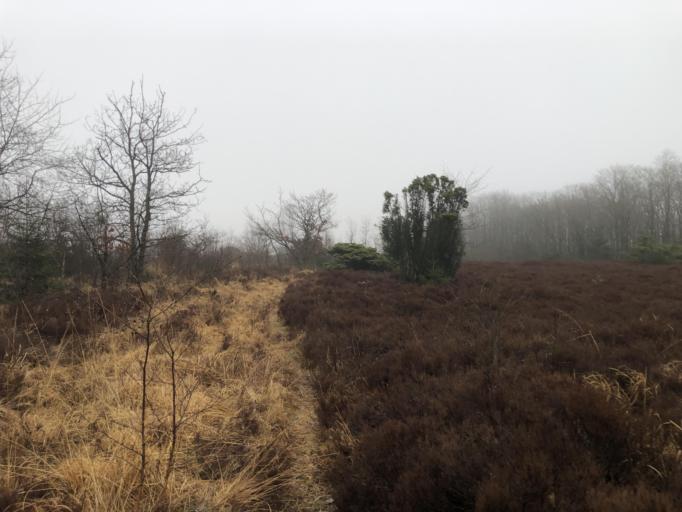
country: DK
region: Central Jutland
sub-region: Holstebro Kommune
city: Holstebro
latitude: 56.2465
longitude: 8.5117
